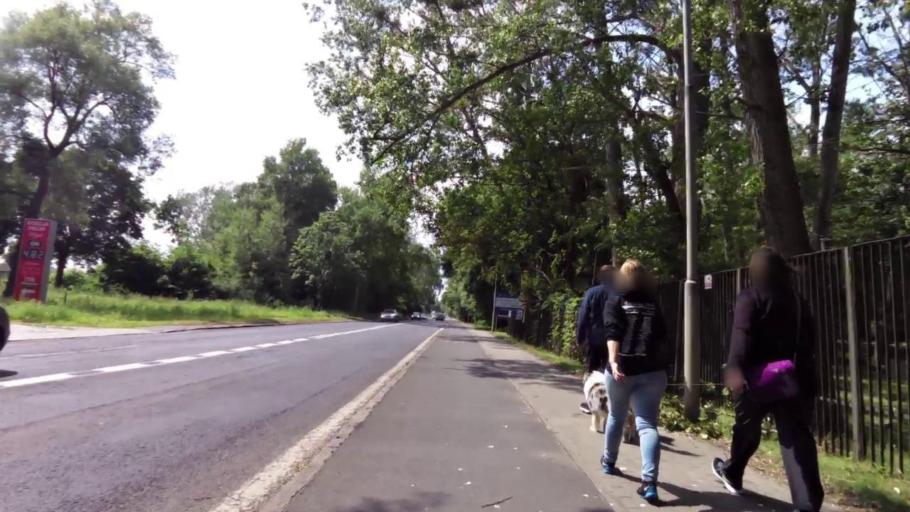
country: PL
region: West Pomeranian Voivodeship
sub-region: Szczecin
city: Szczecin
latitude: 53.3965
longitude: 14.6248
